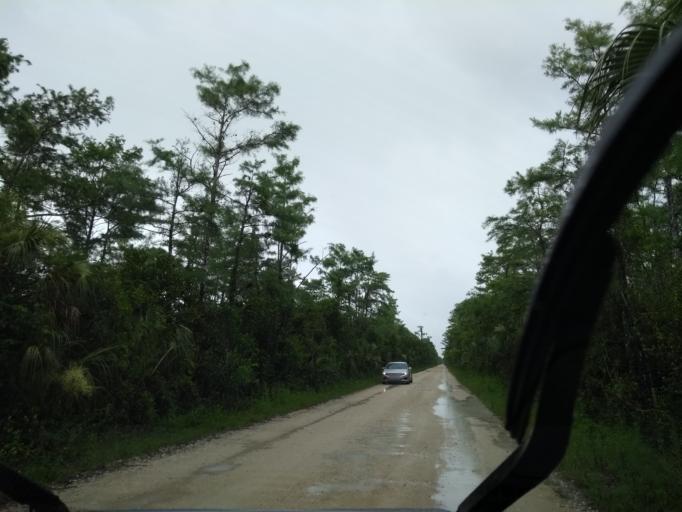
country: US
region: Florida
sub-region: Miami-Dade County
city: The Hammocks
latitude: 25.7602
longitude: -81.0276
